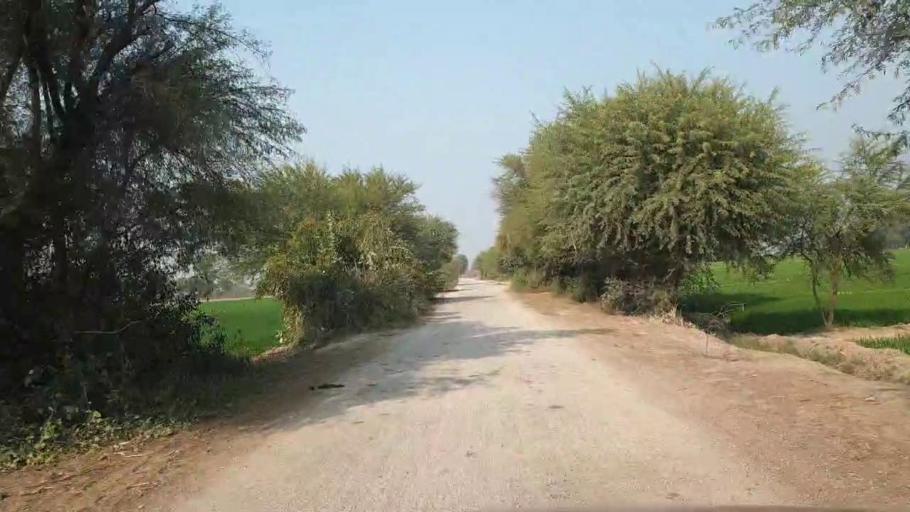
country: PK
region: Sindh
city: Hala
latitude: 25.8492
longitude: 68.4618
